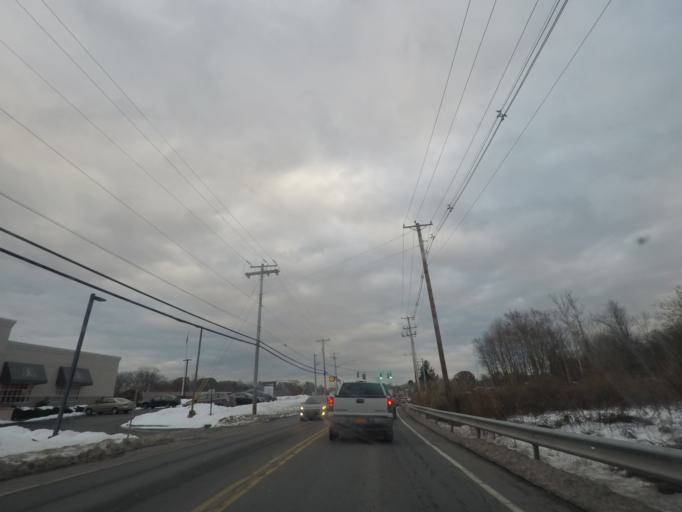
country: US
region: New York
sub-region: Orange County
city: Balmville
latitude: 41.5287
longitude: -74.0347
